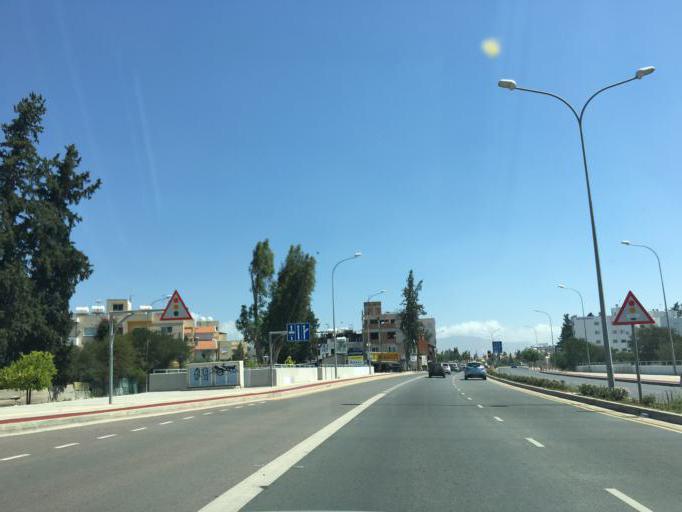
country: CY
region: Lefkosia
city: Nicosia
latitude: 35.1517
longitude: 33.3279
